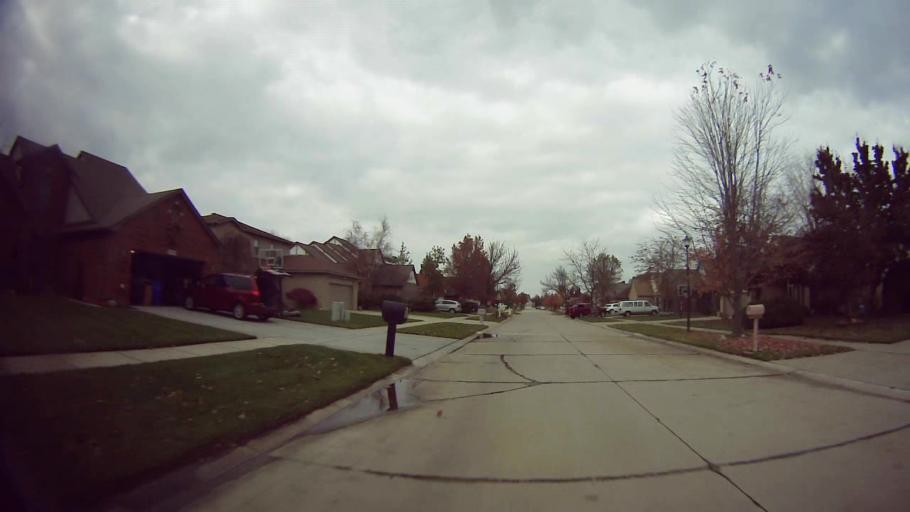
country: US
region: Michigan
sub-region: Macomb County
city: Fraser
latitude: 42.5421
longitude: -82.9651
